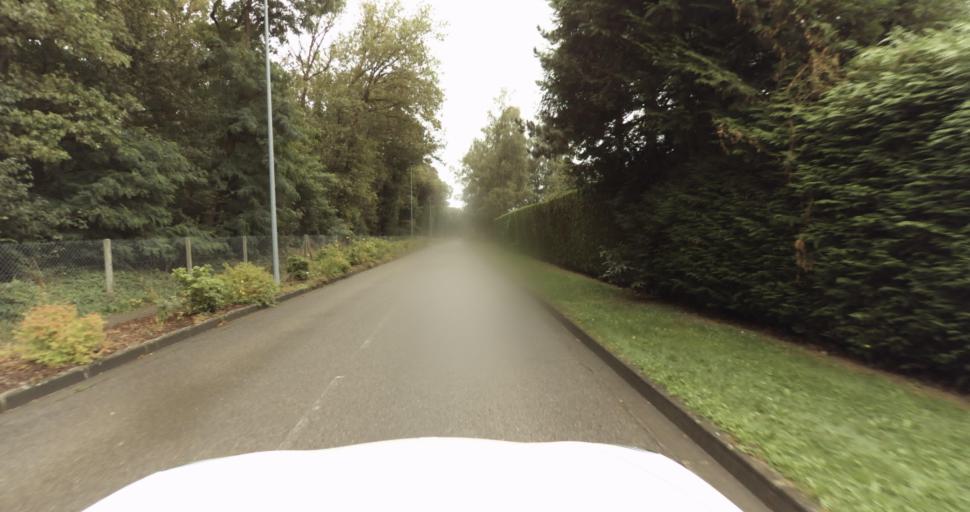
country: FR
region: Haute-Normandie
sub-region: Departement de l'Eure
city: Evreux
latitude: 49.0389
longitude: 1.1370
